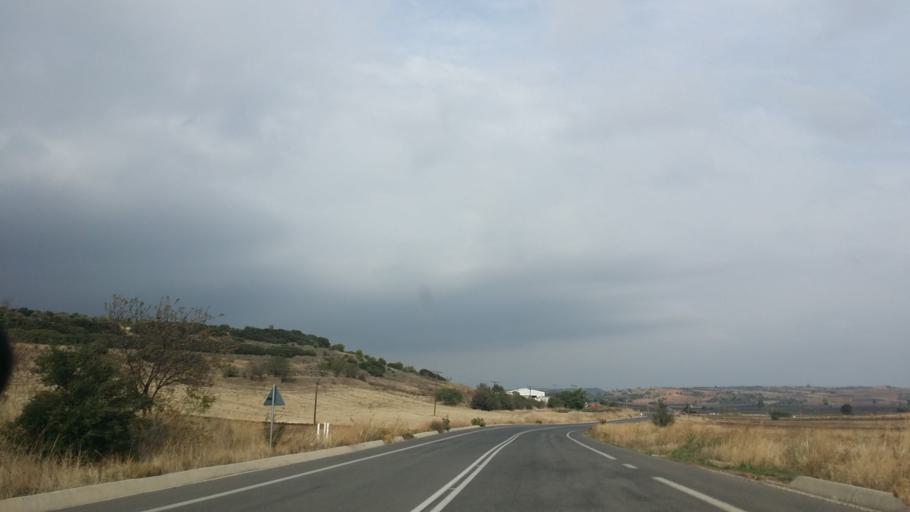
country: GR
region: Central Greece
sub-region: Nomos Voiotias
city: Thespies
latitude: 38.2798
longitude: 23.1211
